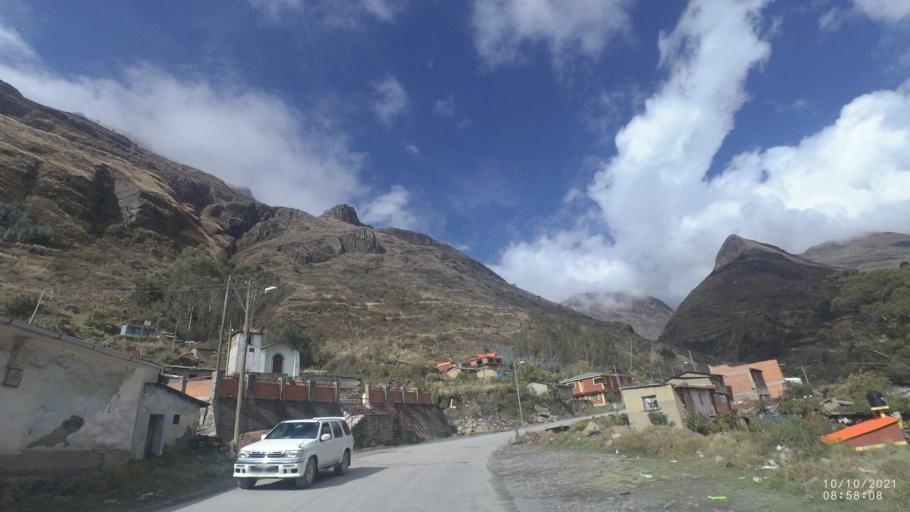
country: BO
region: La Paz
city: Quime
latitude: -16.9979
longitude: -67.2550
